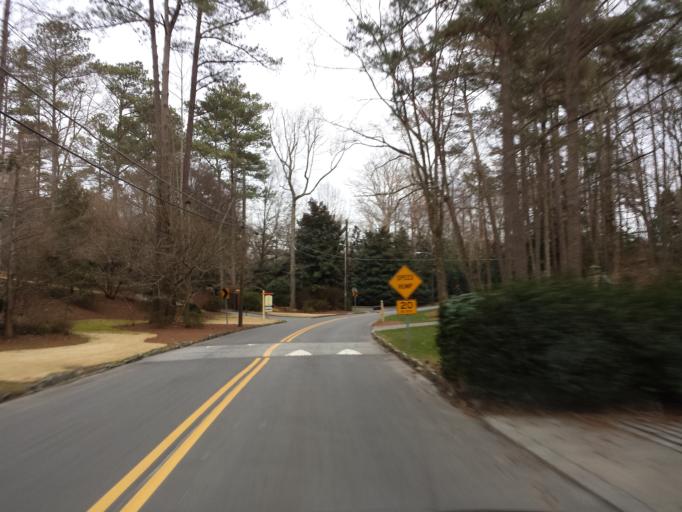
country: US
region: Georgia
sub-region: Cobb County
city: Vinings
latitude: 33.8838
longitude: -84.4194
